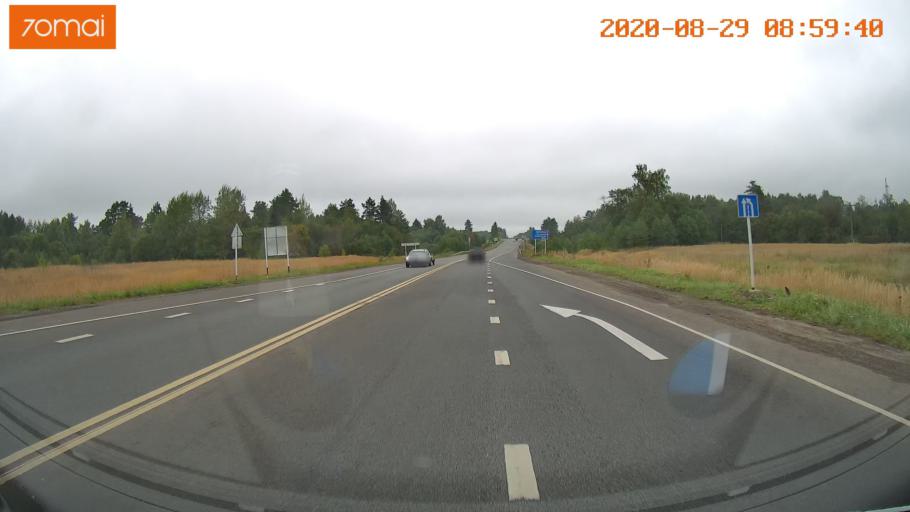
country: RU
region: Ivanovo
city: Staraya Vichuga
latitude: 57.2946
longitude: 41.9075
